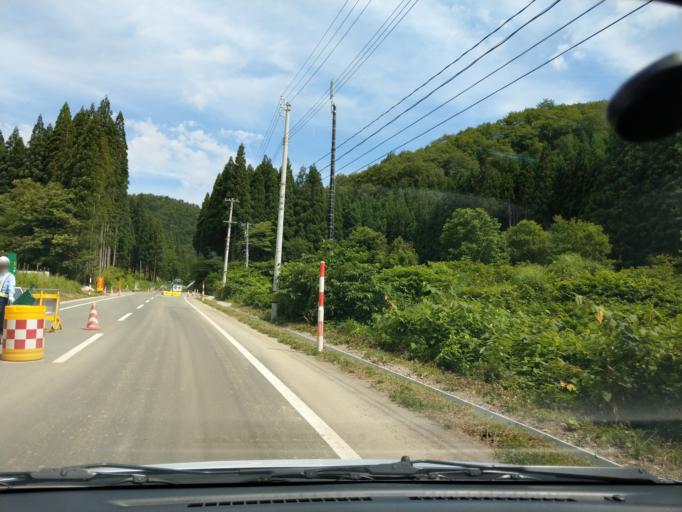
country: JP
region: Akita
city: Kakunodatemachi
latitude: 39.7203
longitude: 140.5846
